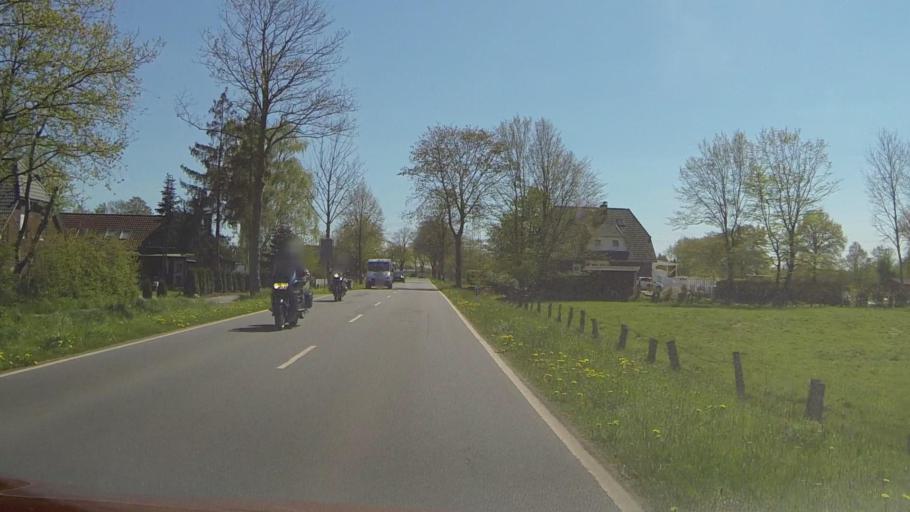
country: DE
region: Schleswig-Holstein
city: Ellerbek
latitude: 53.6539
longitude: 9.8699
